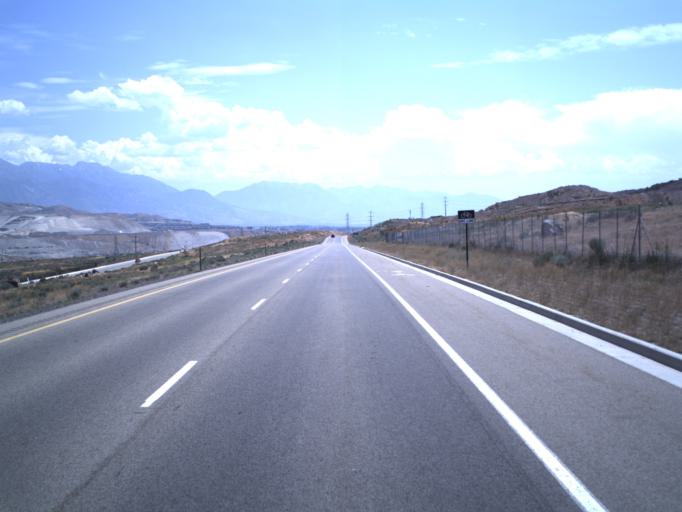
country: US
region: Utah
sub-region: Salt Lake County
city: Bluffdale
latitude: 40.4675
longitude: -111.9631
